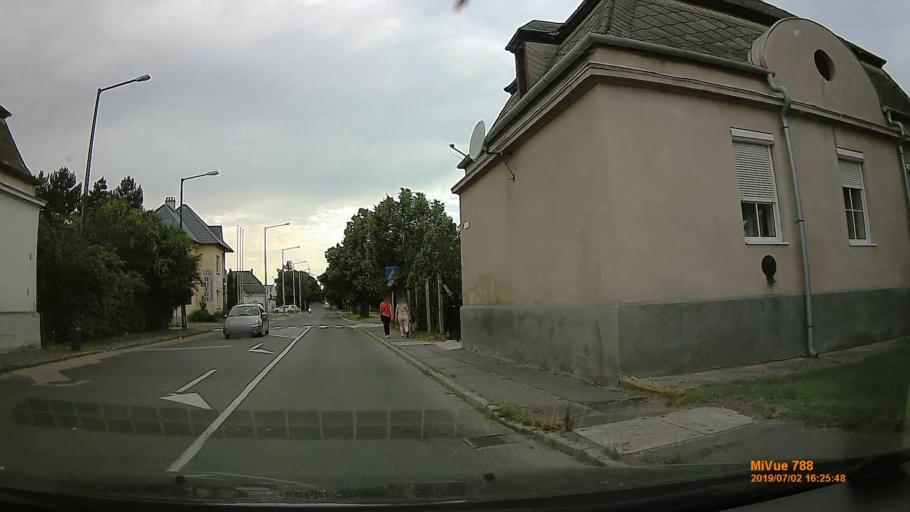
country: HU
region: Gyor-Moson-Sopron
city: Mosonmagyarovar
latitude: 47.8678
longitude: 17.2579
